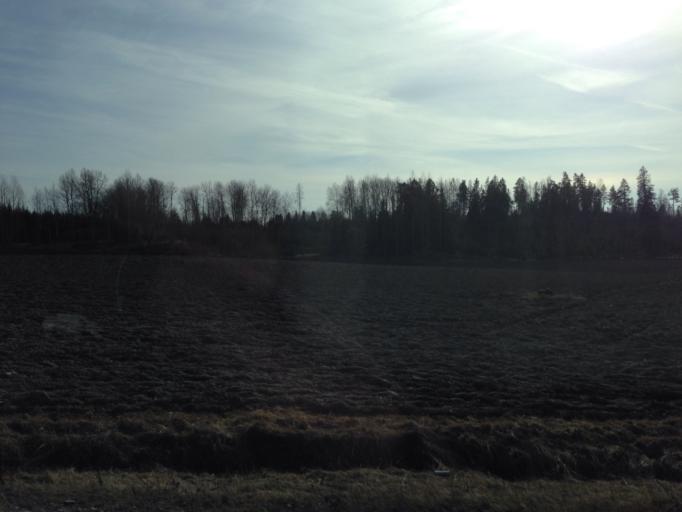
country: SE
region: Soedermanland
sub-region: Flens Kommun
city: Flen
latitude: 59.0368
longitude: 16.5722
